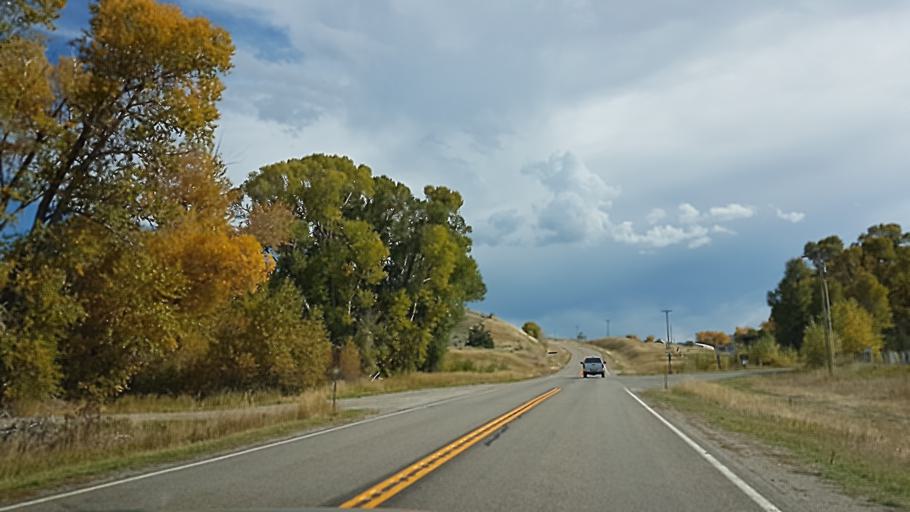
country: US
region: Montana
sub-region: Jefferson County
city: Whitehall
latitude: 45.8036
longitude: -111.9262
